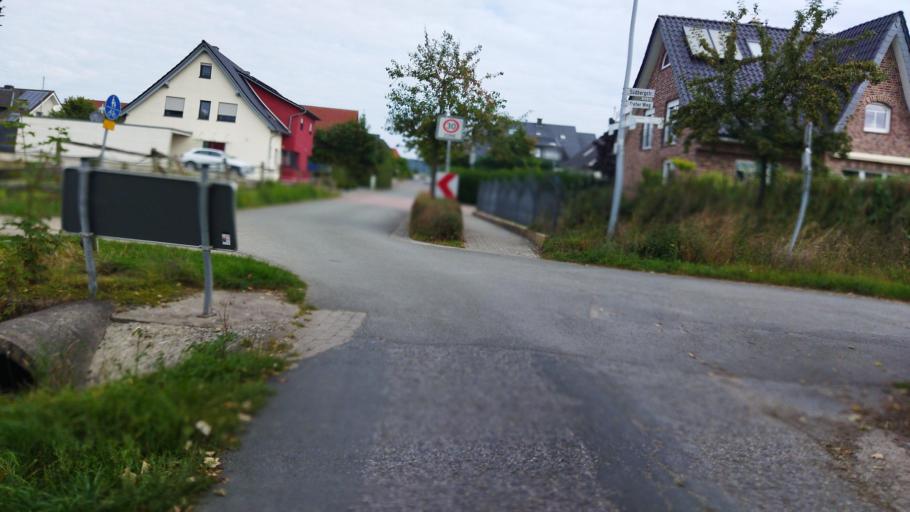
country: DE
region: Lower Saxony
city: Hilter
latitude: 52.1289
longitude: 8.1471
